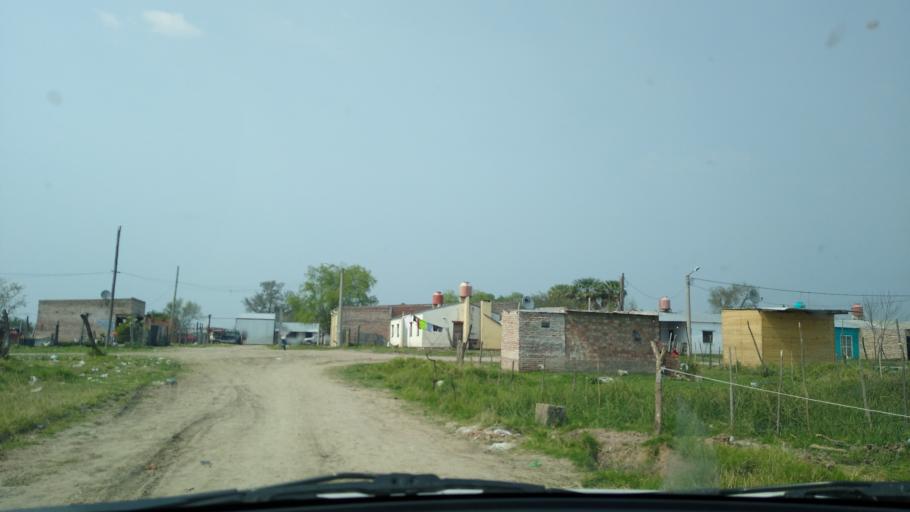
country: AR
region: Chaco
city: Fontana
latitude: -27.4000
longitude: -58.9847
